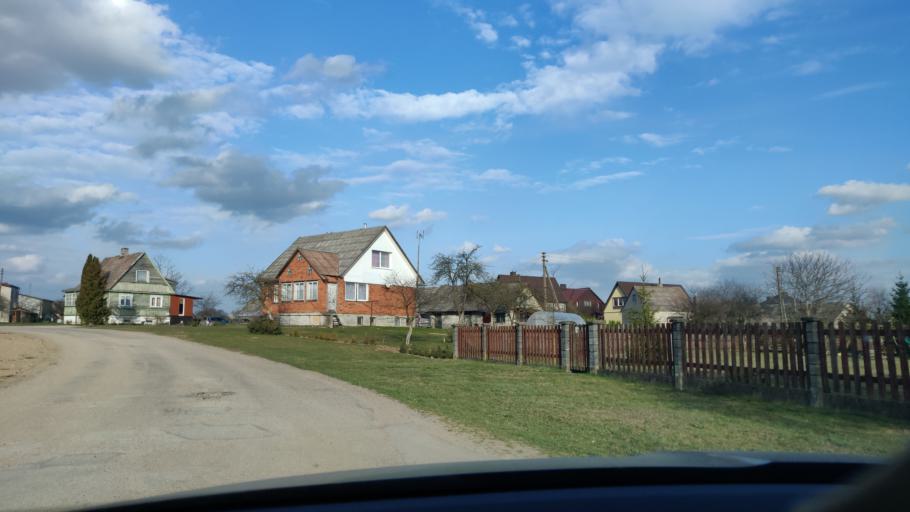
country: LT
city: Trakai
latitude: 54.6060
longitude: 24.9774
